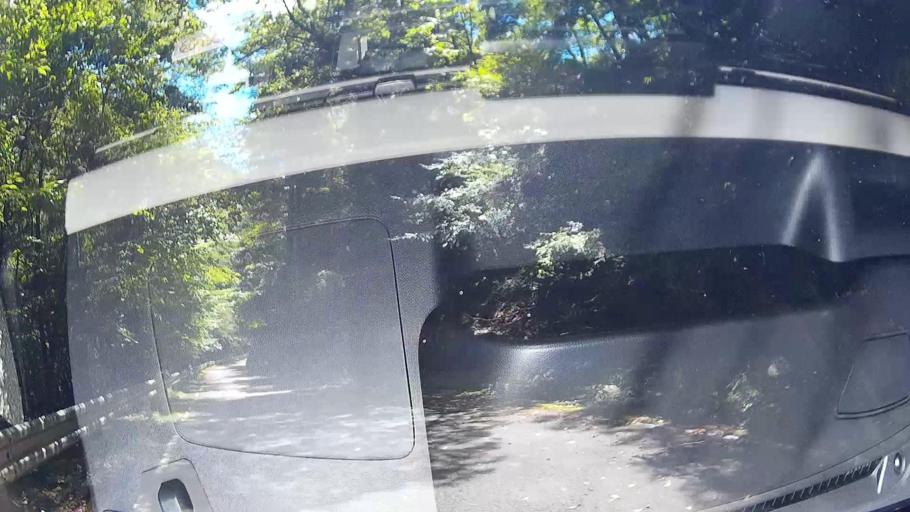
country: JP
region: Shizuoka
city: Fujinomiya
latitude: 35.2914
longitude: 138.3188
